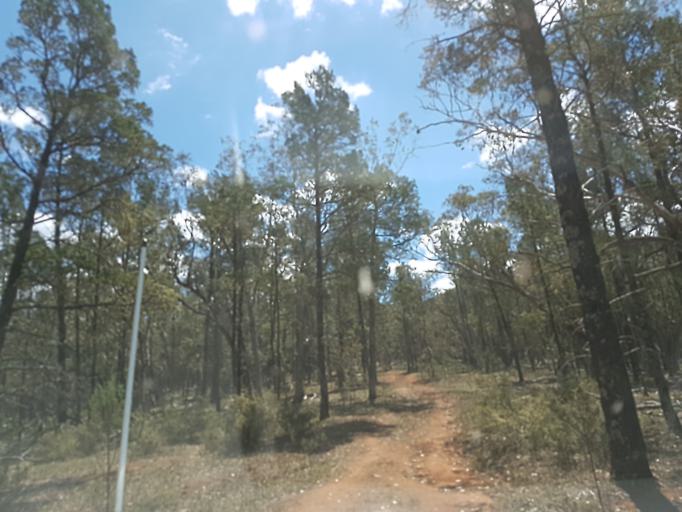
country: AU
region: New South Wales
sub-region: Snowy River
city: Jindabyne
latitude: -36.9420
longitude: 148.3919
